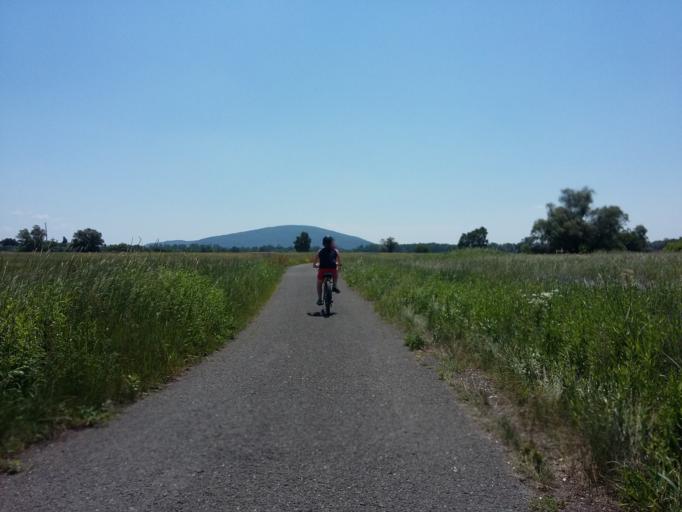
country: AT
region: Lower Austria
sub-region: Politischer Bezirk Ganserndorf
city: Marchegg
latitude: 48.2551
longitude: 16.9529
